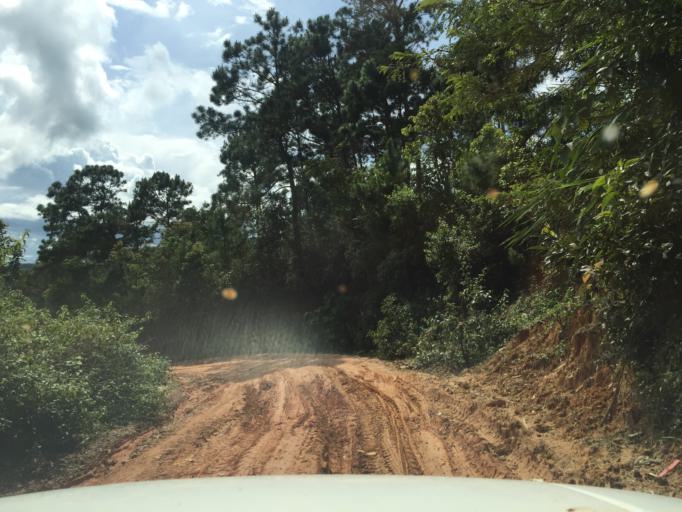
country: LA
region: Xiangkhoang
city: Muang Phonsavan
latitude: 19.3328
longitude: 103.4775
